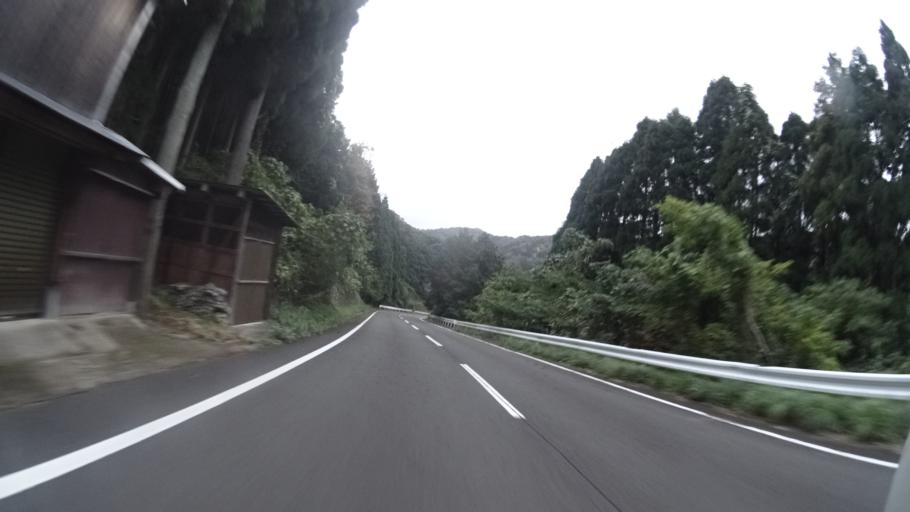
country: JP
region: Kyoto
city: Maizuru
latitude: 35.5646
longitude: 135.4573
